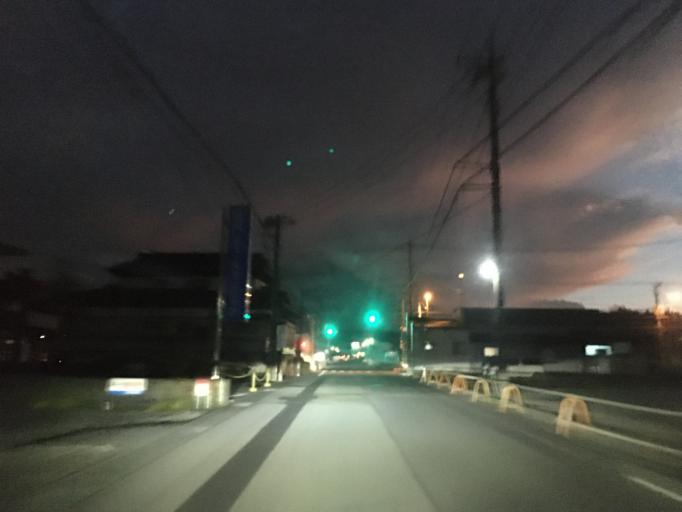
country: JP
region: Yamanashi
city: Fujikawaguchiko
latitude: 35.4762
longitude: 138.7912
